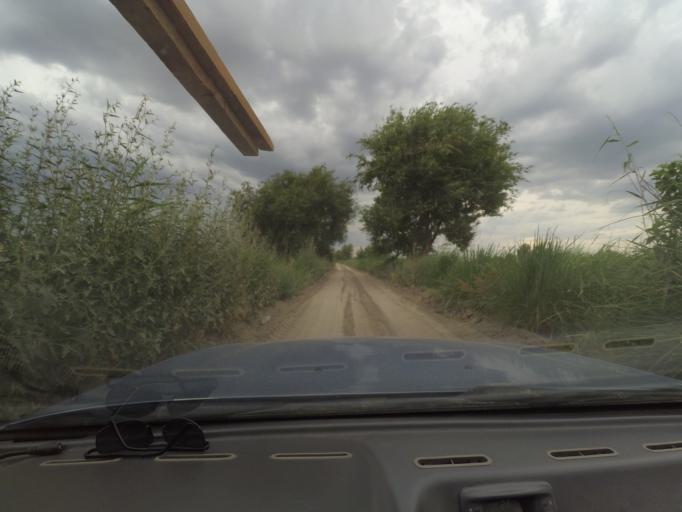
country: TJ
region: Viloyati Sughd
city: Buston
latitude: 40.5499
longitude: 69.0774
